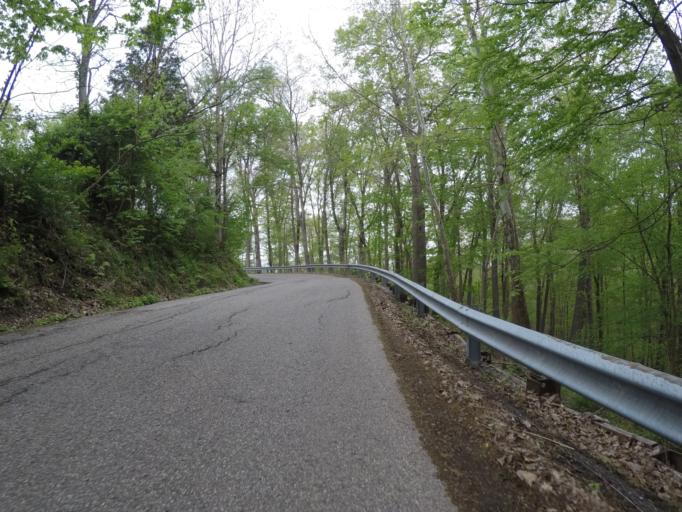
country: US
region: West Virginia
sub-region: Cabell County
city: Barboursville
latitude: 38.4005
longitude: -82.2639
